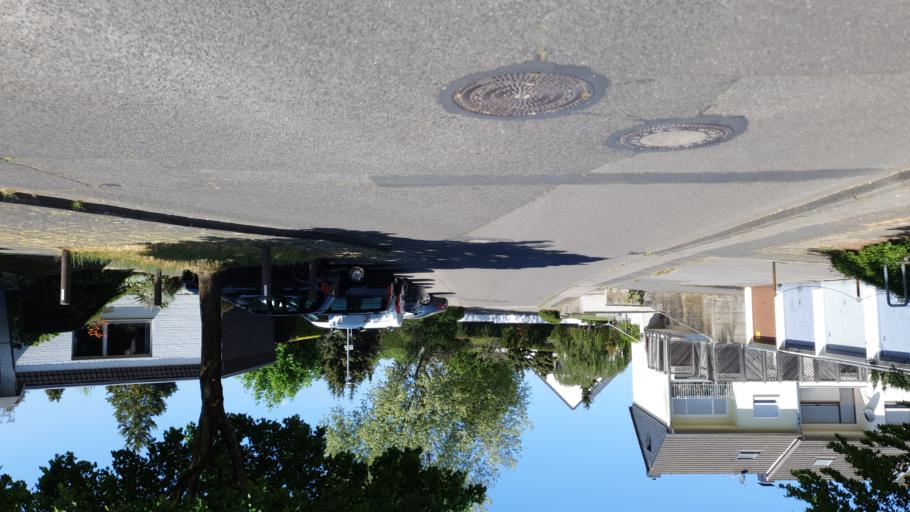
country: DE
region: North Rhine-Westphalia
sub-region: Regierungsbezirk Koln
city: Odenthal
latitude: 51.0019
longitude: 7.0941
